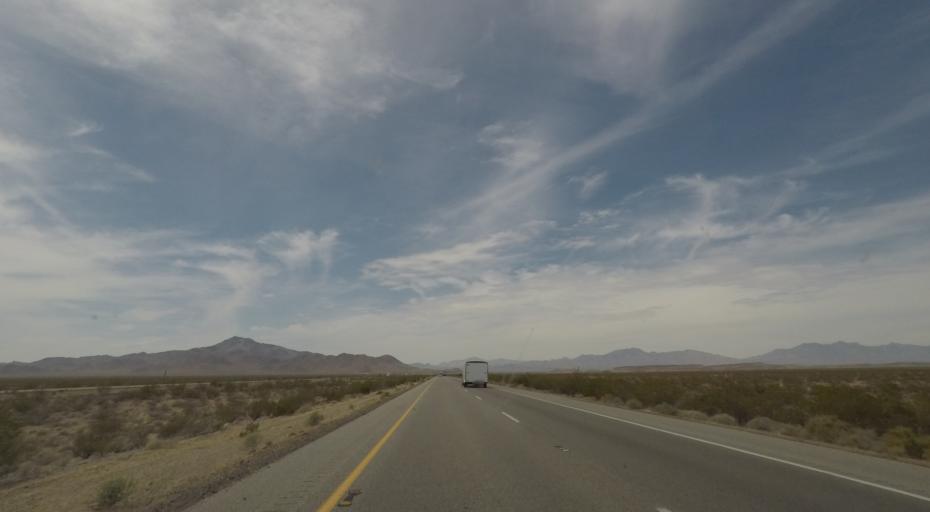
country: US
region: California
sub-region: San Bernardino County
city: Needles
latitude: 34.8058
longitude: -115.2640
